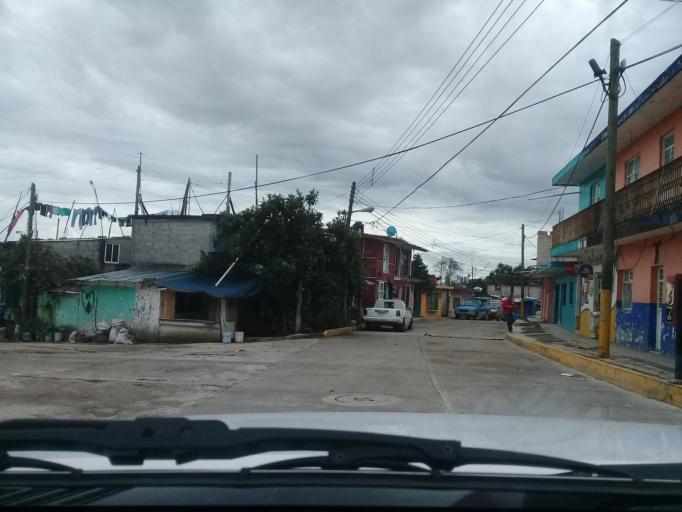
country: MX
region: Veracruz
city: Rafael Lucio
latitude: 19.5949
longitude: -96.9885
